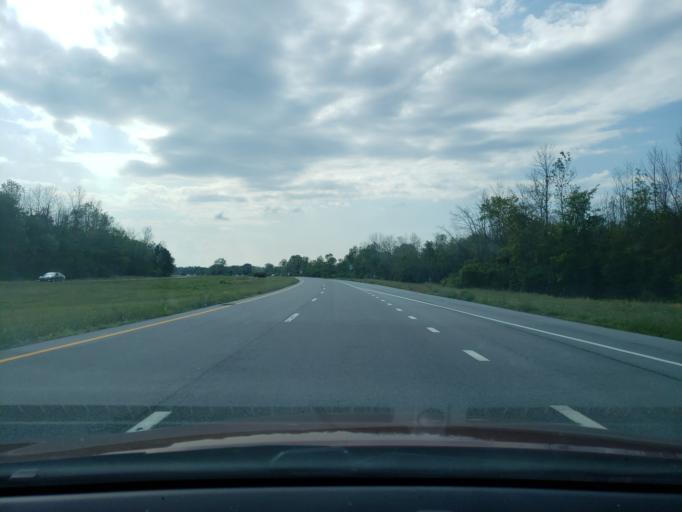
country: US
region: New York
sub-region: Monroe County
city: Greece
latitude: 43.2726
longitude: -77.6708
